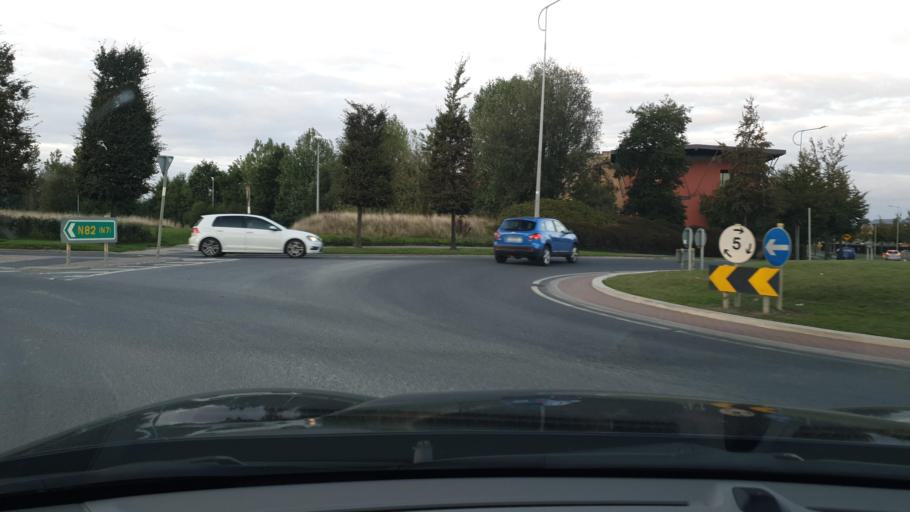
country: IE
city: Jobstown
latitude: 53.2880
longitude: -6.4229
